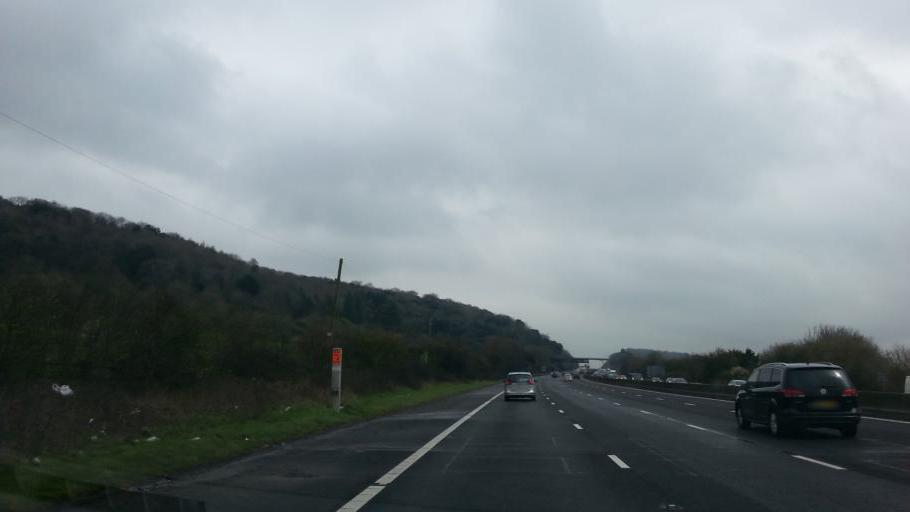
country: GB
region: England
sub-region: North Somerset
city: Clevedon
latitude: 51.4402
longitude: -2.8274
